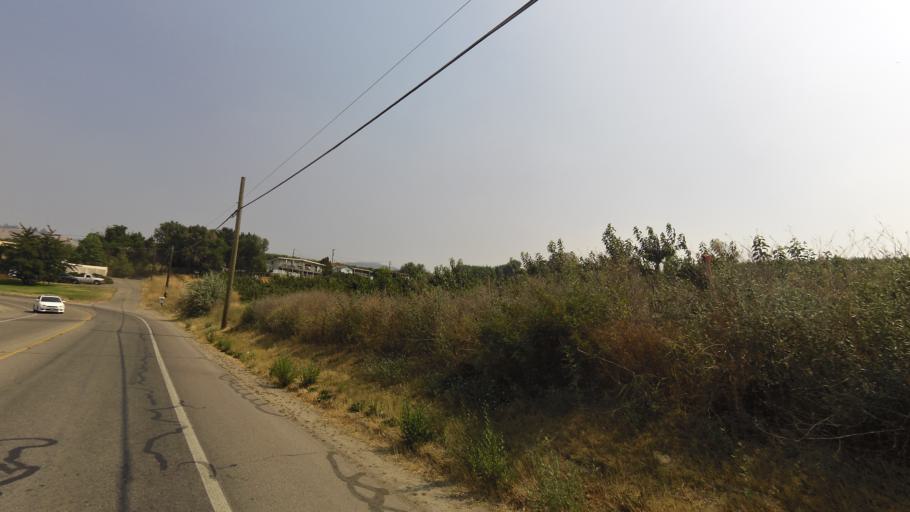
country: CA
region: British Columbia
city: Kelowna
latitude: 49.9181
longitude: -119.3660
